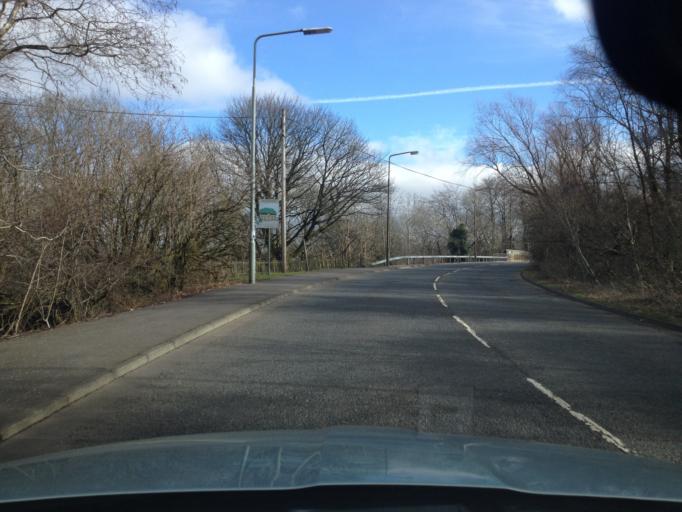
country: GB
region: Scotland
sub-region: West Lothian
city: Livingston
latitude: 55.8648
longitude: -3.5221
